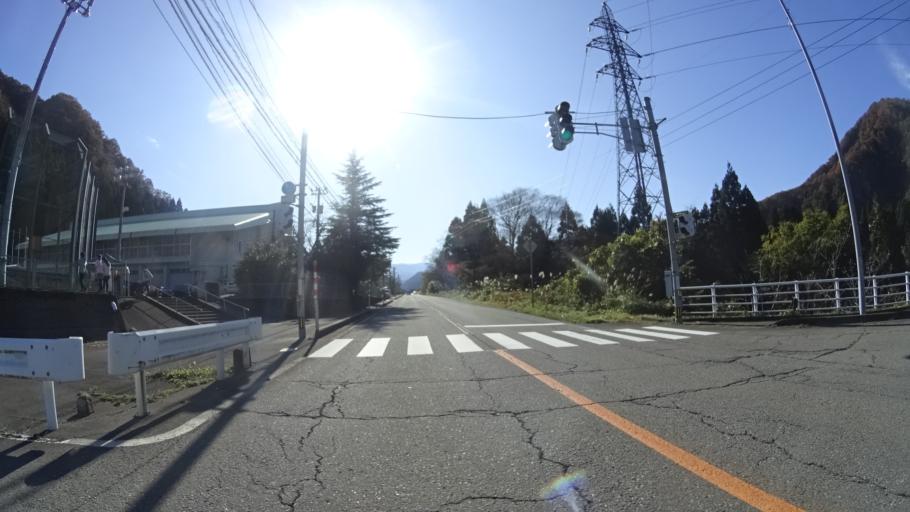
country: JP
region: Ishikawa
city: Tsurugi-asahimachi
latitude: 36.3520
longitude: 136.6245
